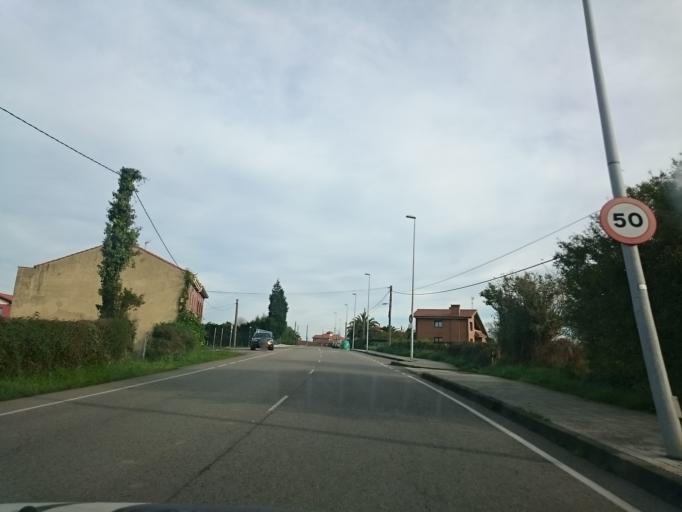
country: ES
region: Asturias
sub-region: Province of Asturias
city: Arriba
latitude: 43.5250
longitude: -5.5890
